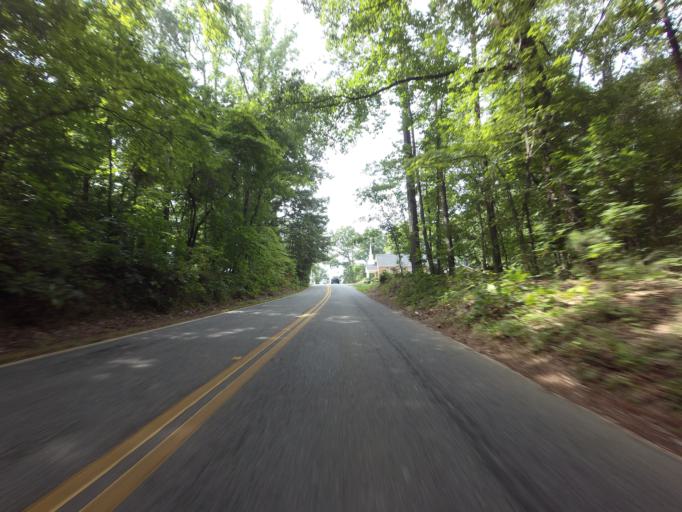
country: US
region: Georgia
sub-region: Gwinnett County
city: Duluth
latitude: 34.0443
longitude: -84.1417
